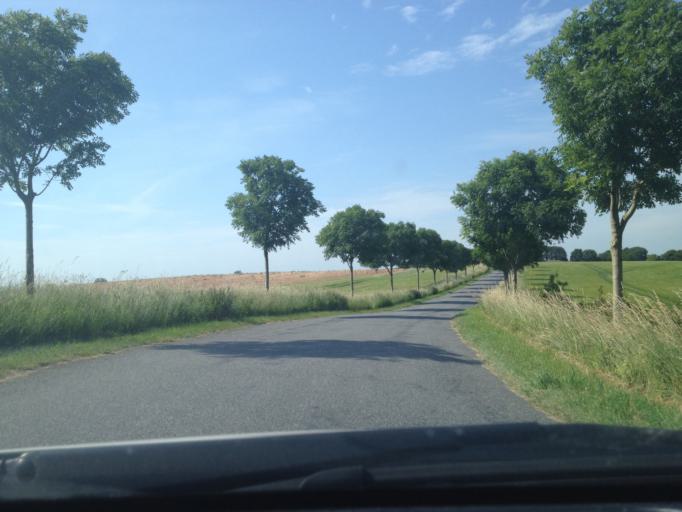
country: DK
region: Central Jutland
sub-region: Samso Kommune
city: Tranebjerg
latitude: 55.7920
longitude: 10.5733
